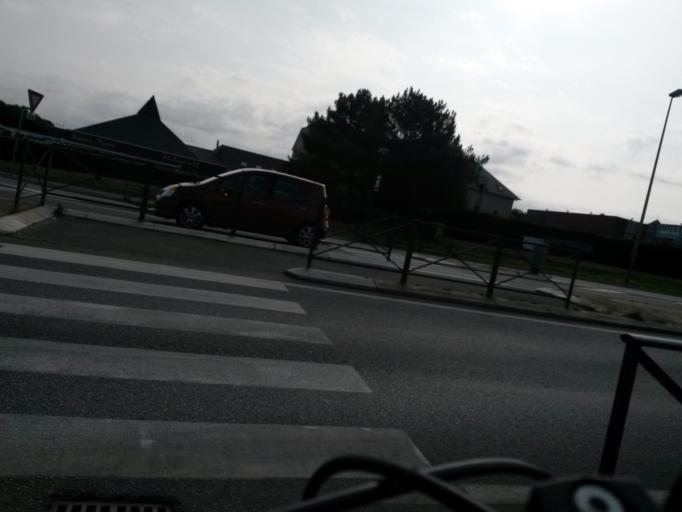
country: FR
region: Pays de la Loire
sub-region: Departement de la Loire-Atlantique
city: Guerande
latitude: 47.3270
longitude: -2.4159
